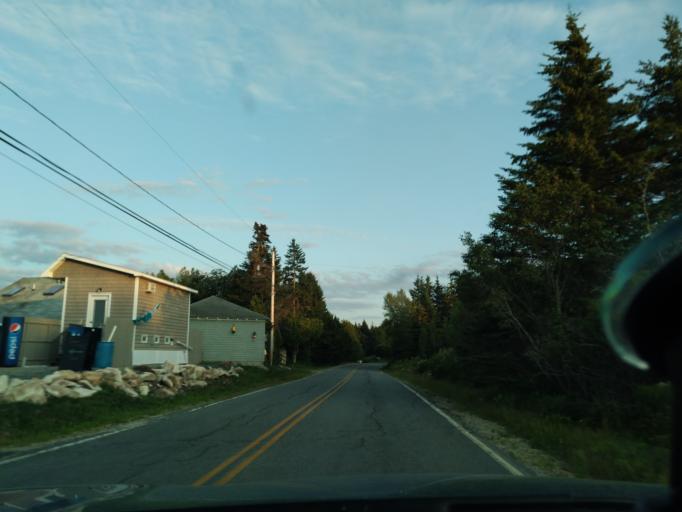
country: US
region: Maine
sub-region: Hancock County
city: Gouldsboro
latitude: 44.3728
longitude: -68.0343
